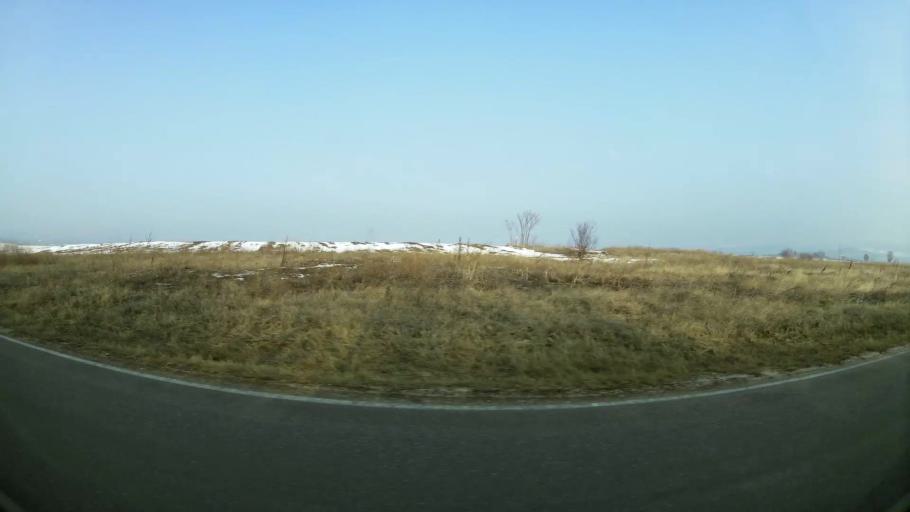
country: MK
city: Miladinovci
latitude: 41.9762
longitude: 21.6307
